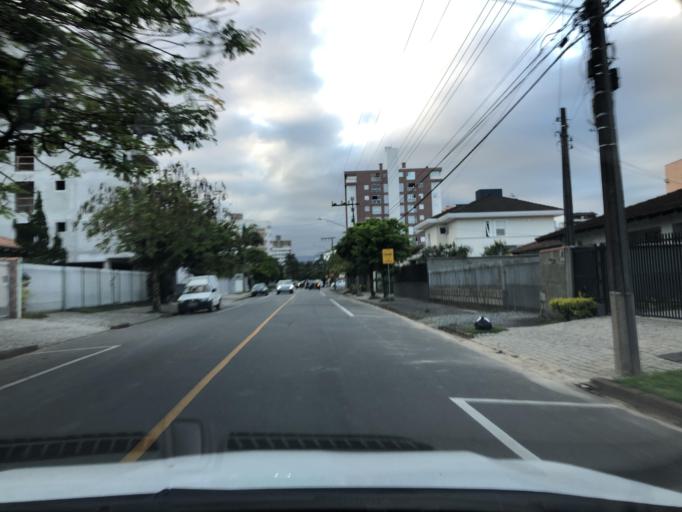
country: BR
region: Santa Catarina
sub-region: Joinville
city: Joinville
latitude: -26.2756
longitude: -48.8534
